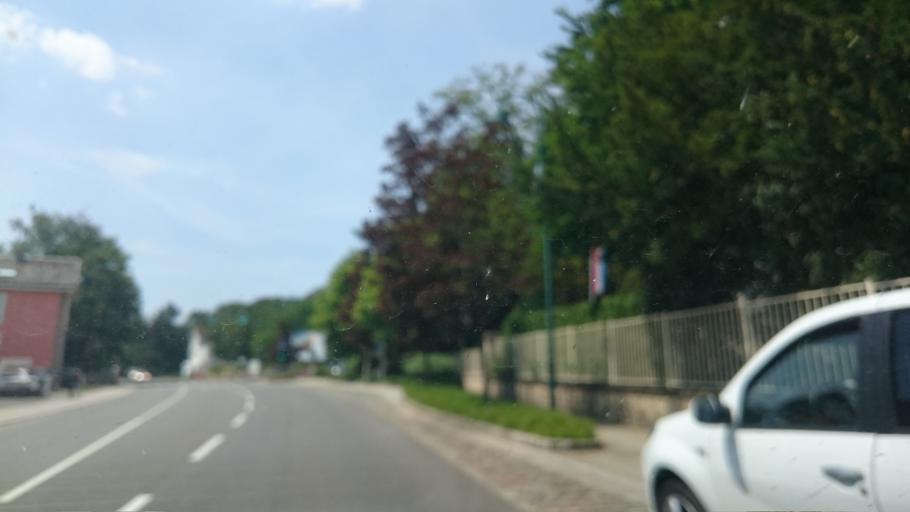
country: LU
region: Luxembourg
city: Capellen
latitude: 49.6459
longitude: 5.9862
